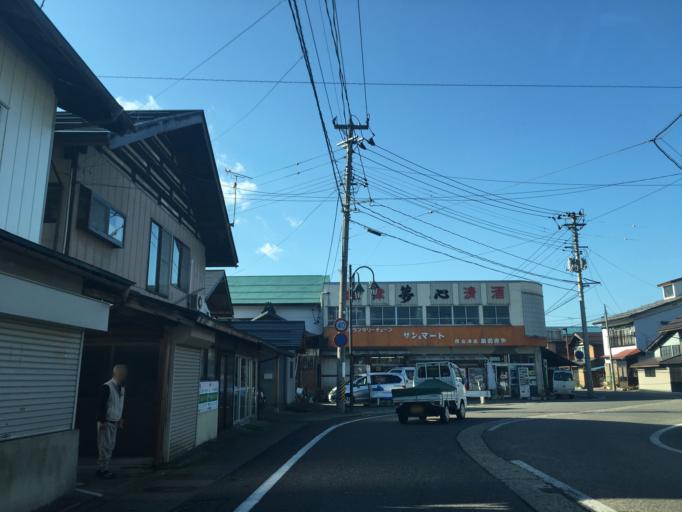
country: JP
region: Fukushima
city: Kitakata
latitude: 37.5842
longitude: 139.6497
